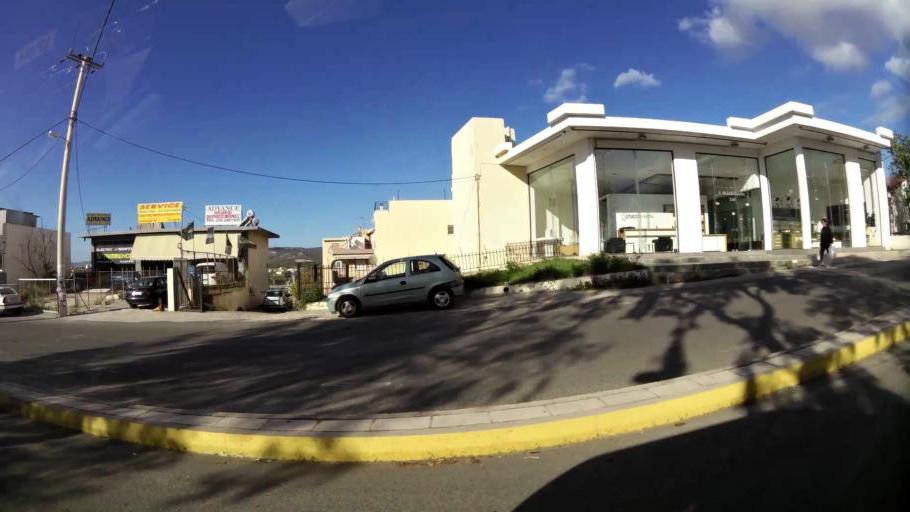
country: GR
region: Attica
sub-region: Nomarchia Anatolikis Attikis
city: Acharnes
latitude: 38.0689
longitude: 23.7391
